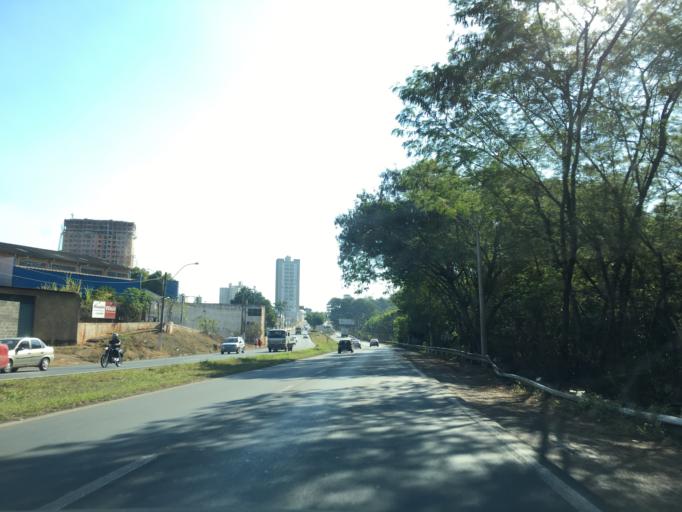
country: BR
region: Sao Paulo
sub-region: Piracicaba
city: Piracicaba
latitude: -22.7165
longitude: -47.6253
